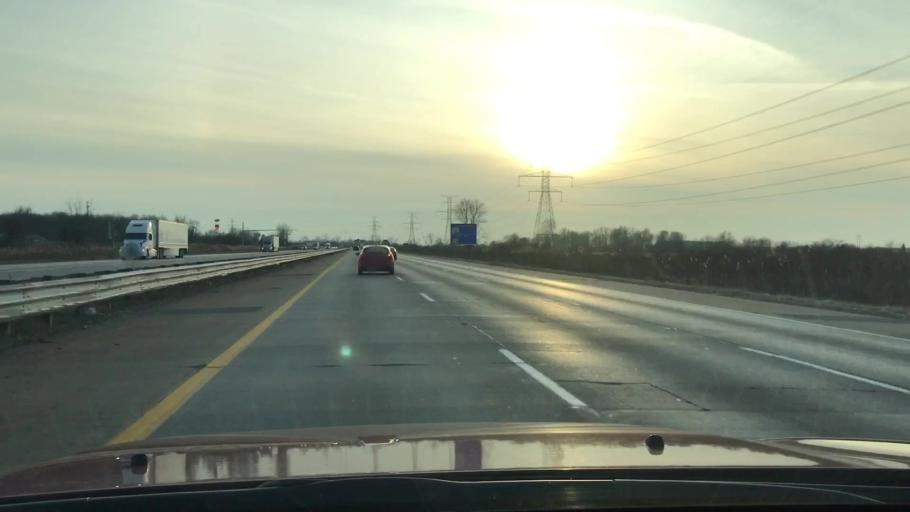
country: US
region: Michigan
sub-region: Monroe County
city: Luna Pier
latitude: 41.8181
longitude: -83.4407
